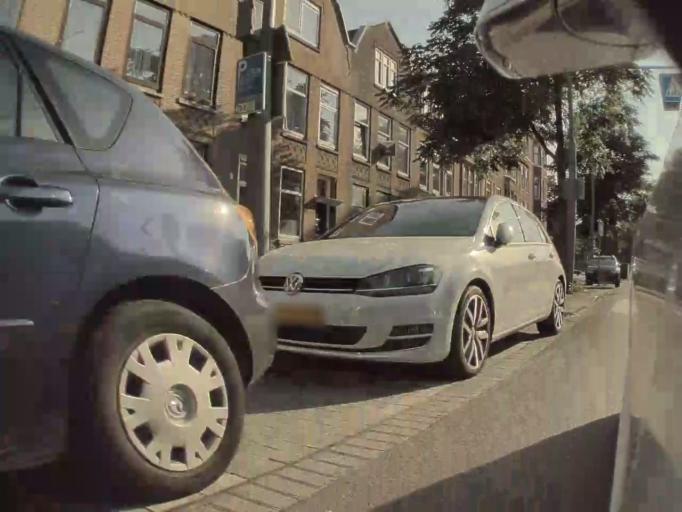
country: NL
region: South Holland
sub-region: Gemeente Rotterdam
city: Delfshaven
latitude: 51.9202
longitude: 4.4497
